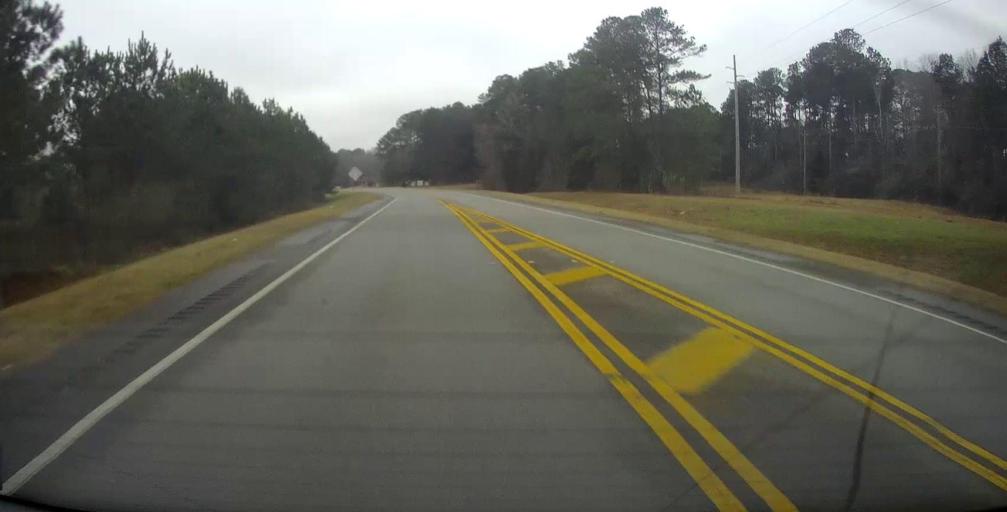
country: US
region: Georgia
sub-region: Lamar County
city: Barnesville
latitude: 33.0532
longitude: -84.1294
